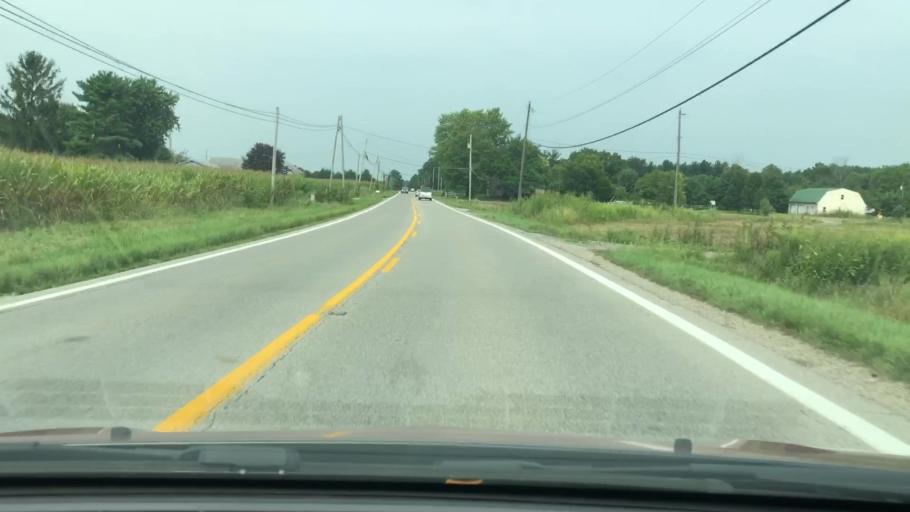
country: US
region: Ohio
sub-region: Delaware County
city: Sunbury
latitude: 40.2338
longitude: -82.8377
